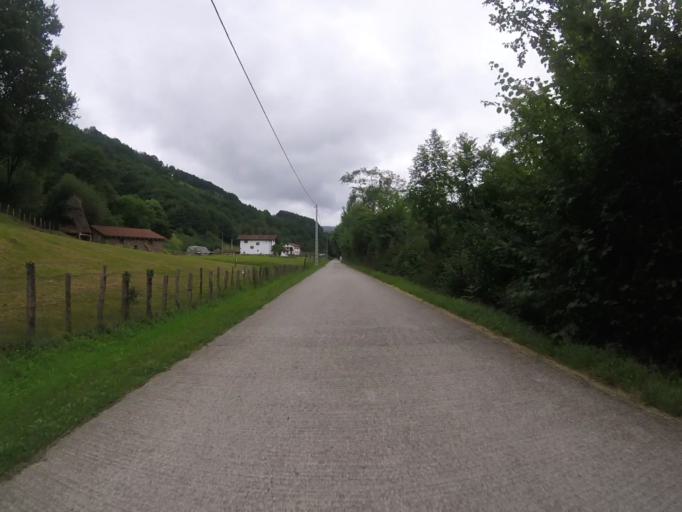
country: ES
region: Navarre
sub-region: Provincia de Navarra
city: Sunbilla
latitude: 43.1529
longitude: -1.6696
